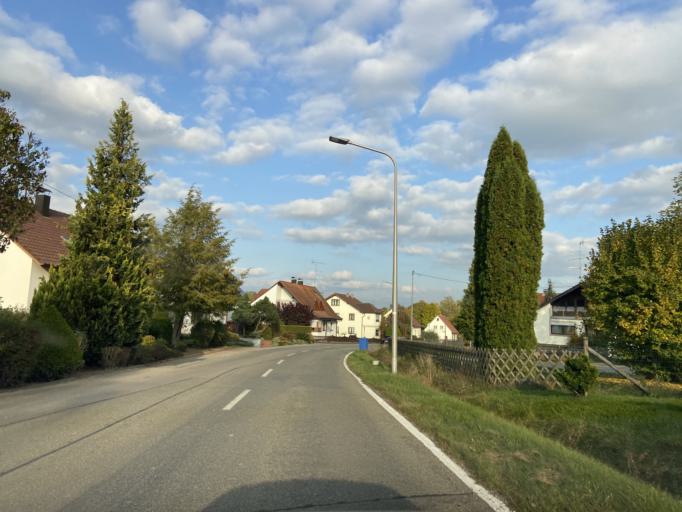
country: DE
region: Baden-Wuerttemberg
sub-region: Tuebingen Region
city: Scheer
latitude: 48.0886
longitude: 9.3227
